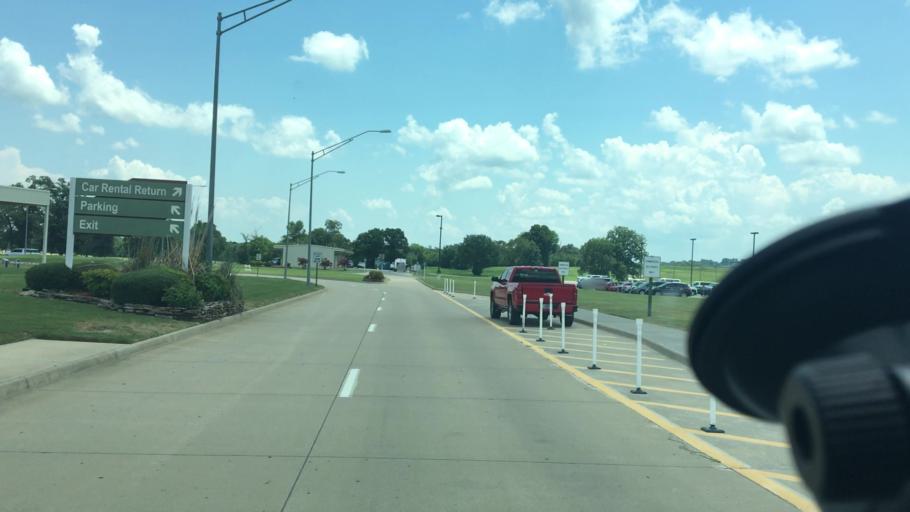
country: US
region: Arkansas
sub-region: Sebastian County
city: Barling
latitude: 35.3413
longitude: -94.3582
